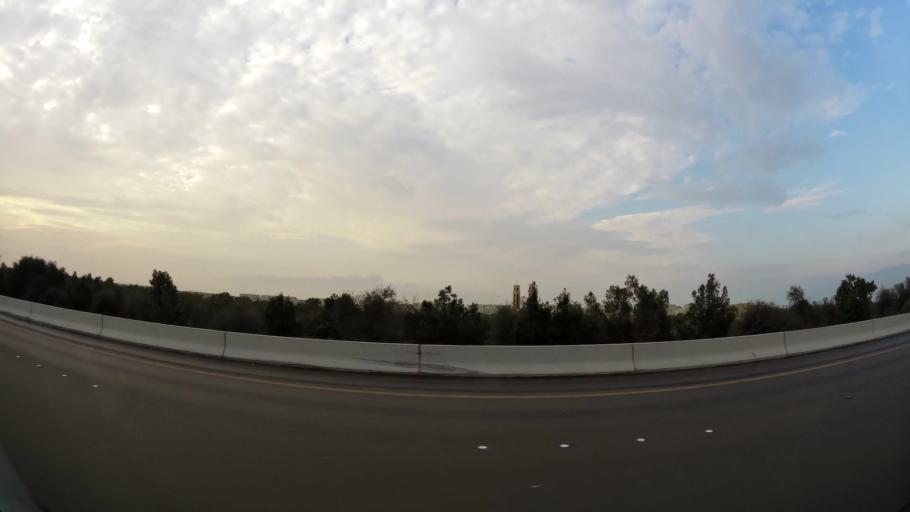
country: AE
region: Abu Dhabi
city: Abu Dhabi
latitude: 24.4022
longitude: 54.4901
